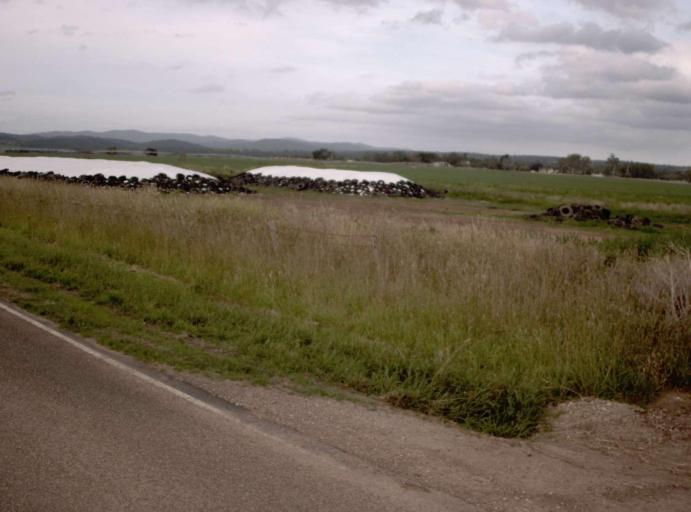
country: AU
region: Victoria
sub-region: Wellington
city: Sale
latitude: -37.8490
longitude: 147.0544
